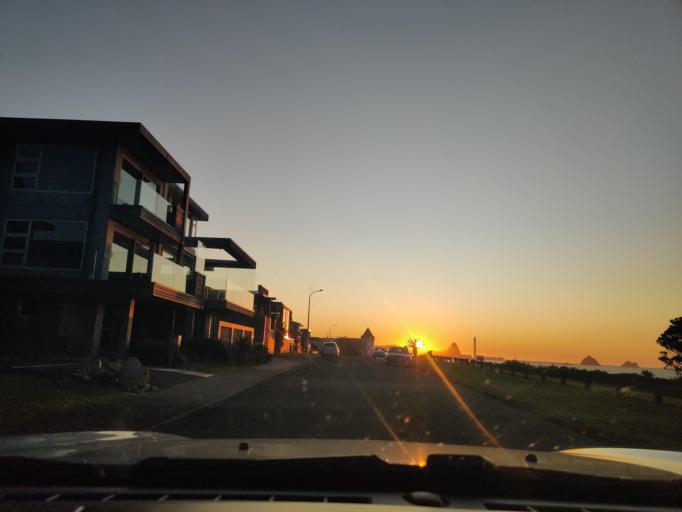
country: NZ
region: Taranaki
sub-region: New Plymouth District
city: New Plymouth
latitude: -39.0513
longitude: 174.0832
